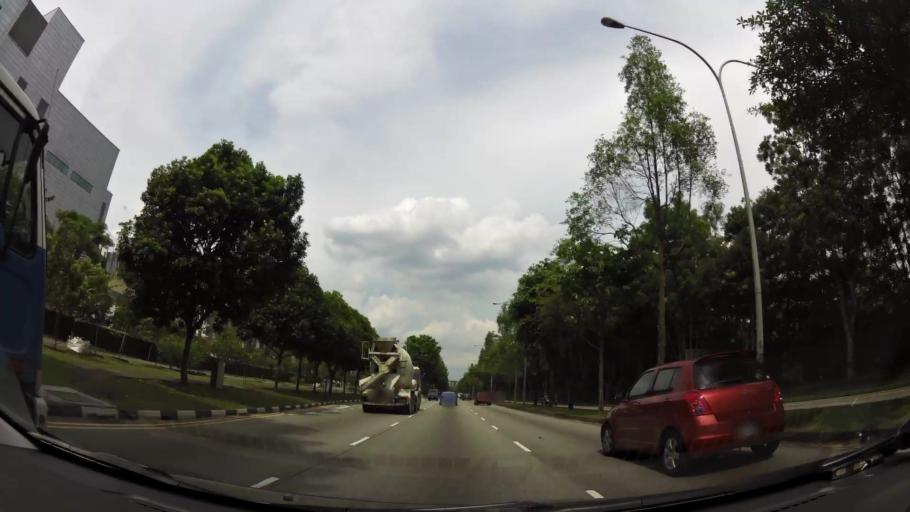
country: MY
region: Johor
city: Johor Bahru
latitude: 1.4333
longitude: 103.8043
